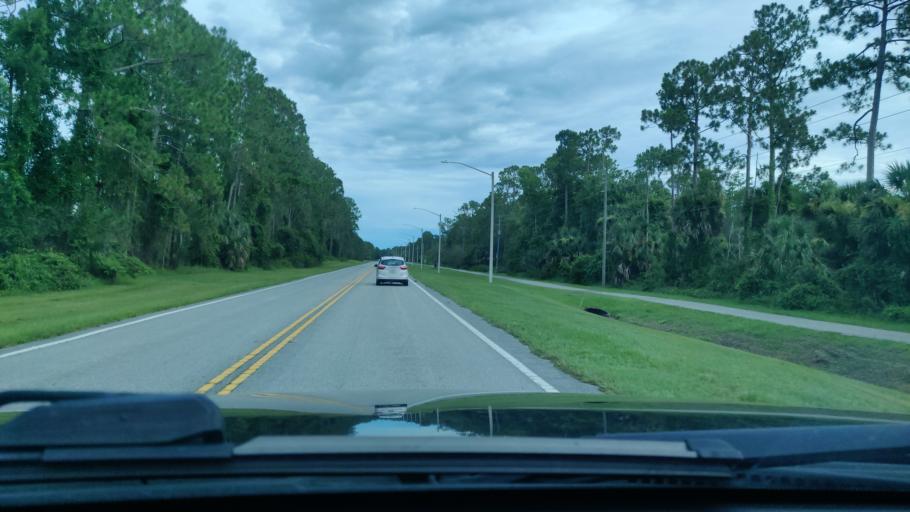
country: US
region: Florida
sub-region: Flagler County
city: Palm Coast
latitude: 29.5451
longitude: -81.2559
